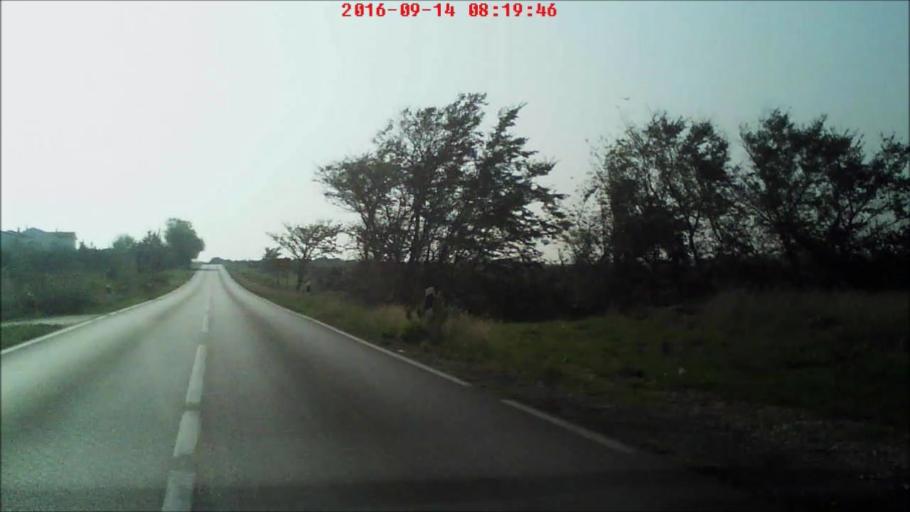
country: HR
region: Zadarska
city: Nin
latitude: 44.2303
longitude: 15.1938
